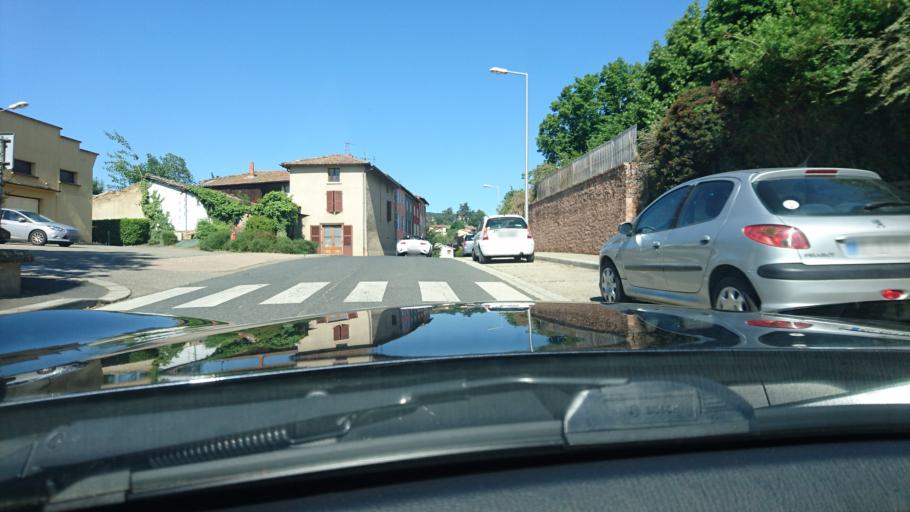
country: FR
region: Rhone-Alpes
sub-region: Departement du Rhone
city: Bessenay
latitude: 45.7759
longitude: 4.5514
